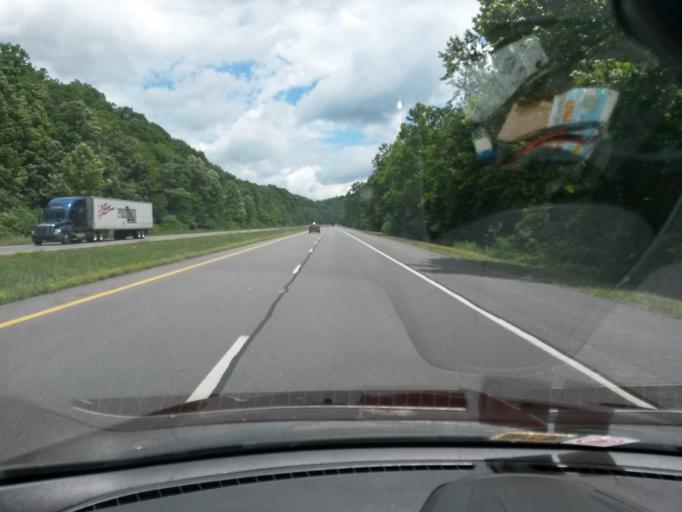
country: US
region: West Virginia
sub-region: Mercer County
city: Athens
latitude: 37.3443
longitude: -80.9517
